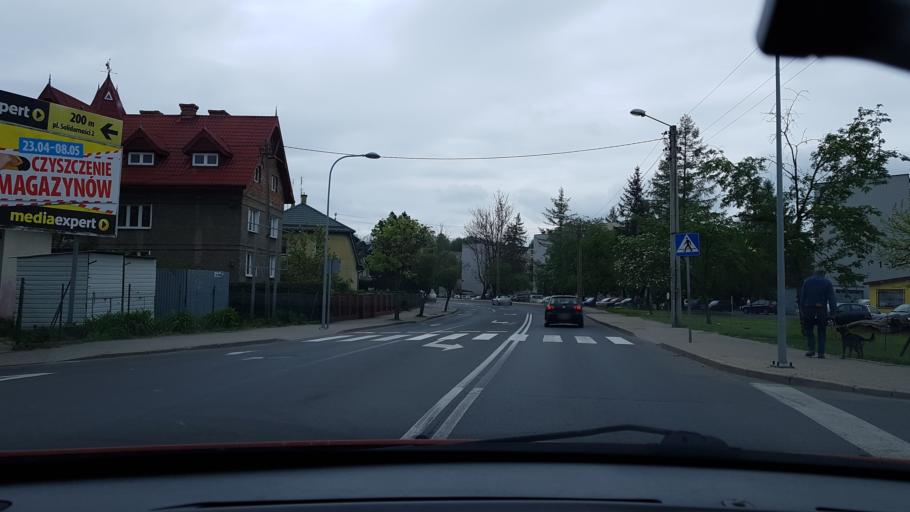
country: PL
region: Opole Voivodeship
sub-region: Powiat nyski
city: Glucholazy
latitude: 50.3164
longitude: 17.3798
